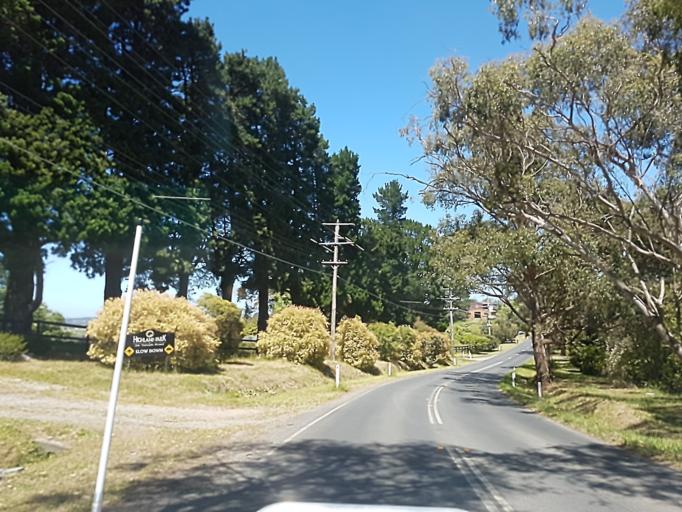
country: AU
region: Victoria
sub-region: Yarra Ranges
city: Selby
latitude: -37.9313
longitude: 145.3695
